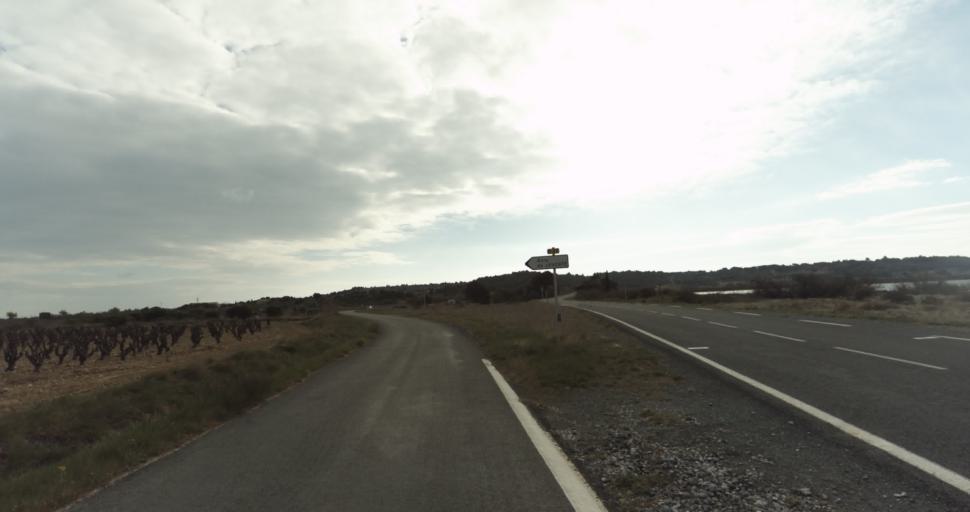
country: FR
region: Languedoc-Roussillon
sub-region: Departement de l'Aude
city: Leucate
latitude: 42.9296
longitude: 3.0047
